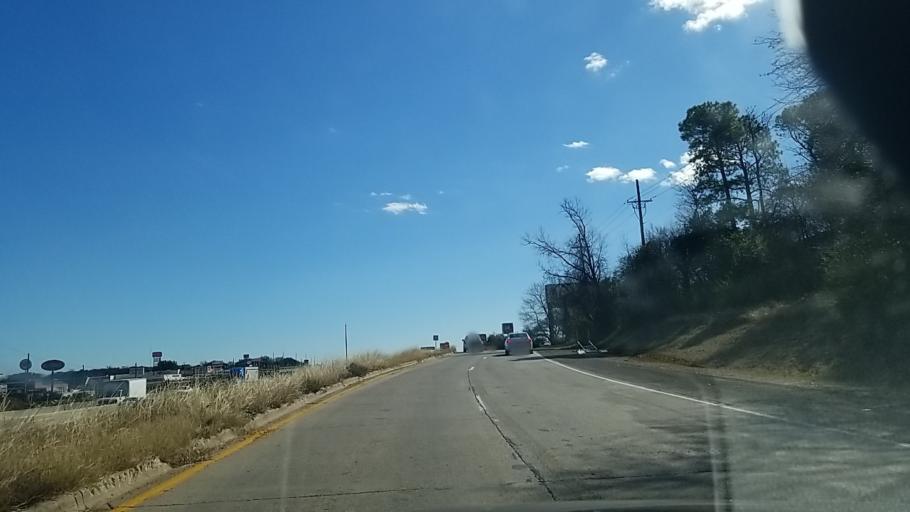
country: US
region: Texas
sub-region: Denton County
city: Denton
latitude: 33.1882
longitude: -97.1106
